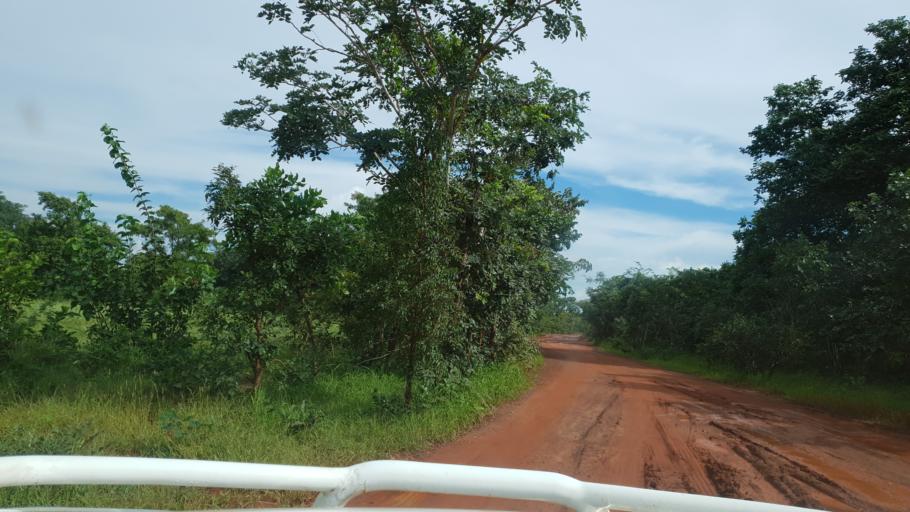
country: ML
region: Sikasso
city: Kolondieba
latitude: 10.7419
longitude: -6.9108
